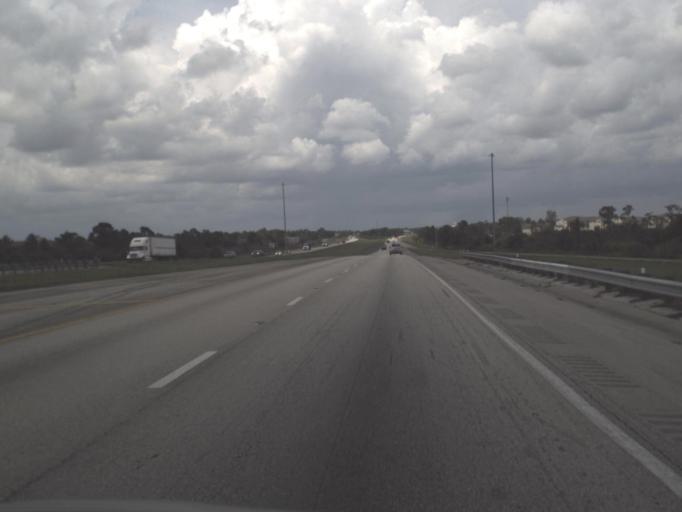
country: US
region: Florida
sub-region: Charlotte County
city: Harbour Heights
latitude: 26.9804
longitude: -82.0238
